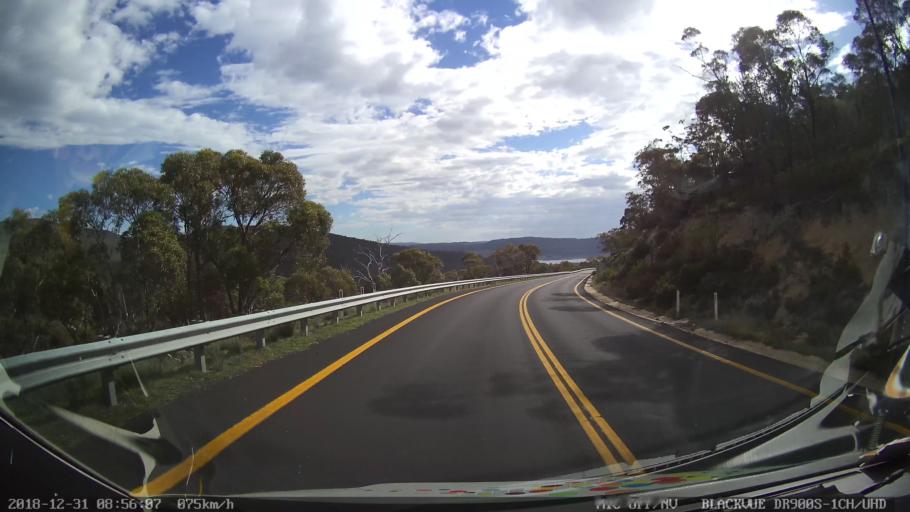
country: AU
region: New South Wales
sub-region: Snowy River
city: Jindabyne
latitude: -36.3428
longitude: 148.5762
